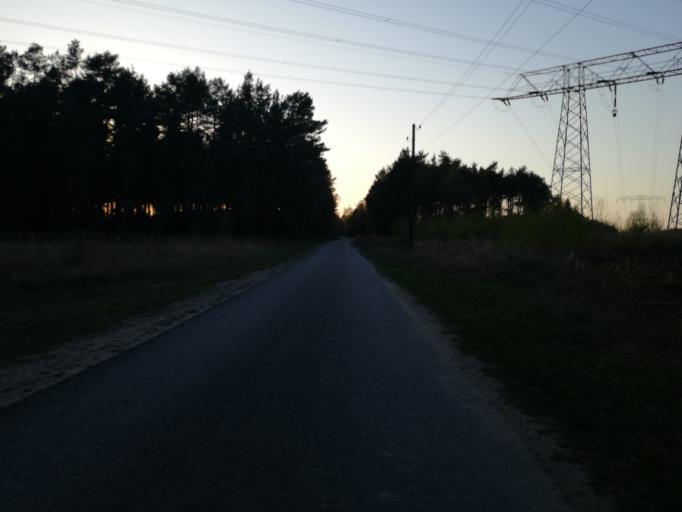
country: DE
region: Brandenburg
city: Calau
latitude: 51.7378
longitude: 13.9934
